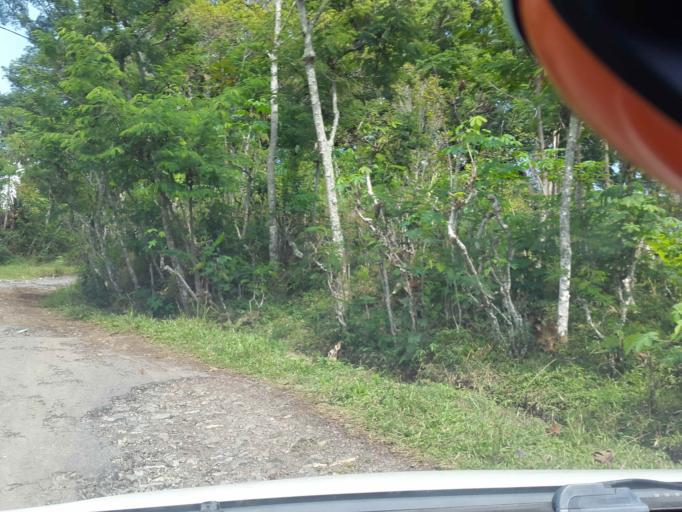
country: ID
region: East Java
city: Ponorogo
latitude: -7.7966
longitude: 111.6486
